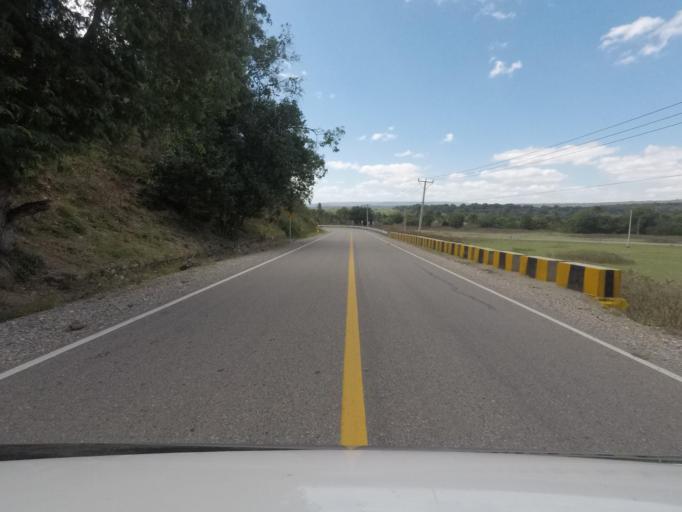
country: TL
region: Lautem
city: Lospalos
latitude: -8.4029
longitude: 126.8294
